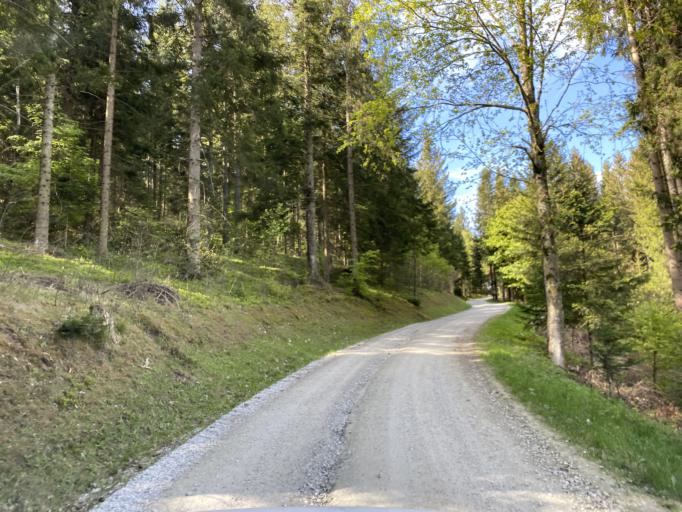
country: AT
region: Styria
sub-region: Politischer Bezirk Weiz
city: Gschaid bei Birkfeld
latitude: 47.3391
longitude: 15.7183
